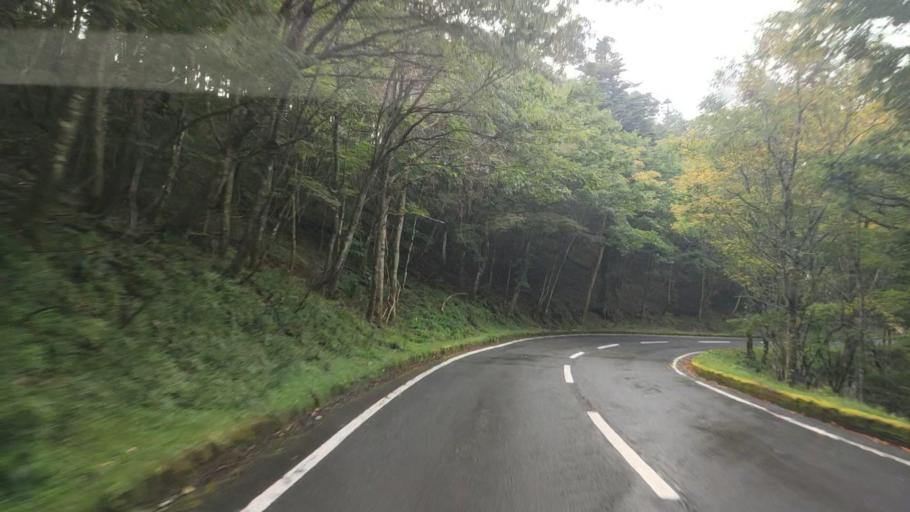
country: JP
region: Shizuoka
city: Fuji
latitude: 35.3111
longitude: 138.7422
